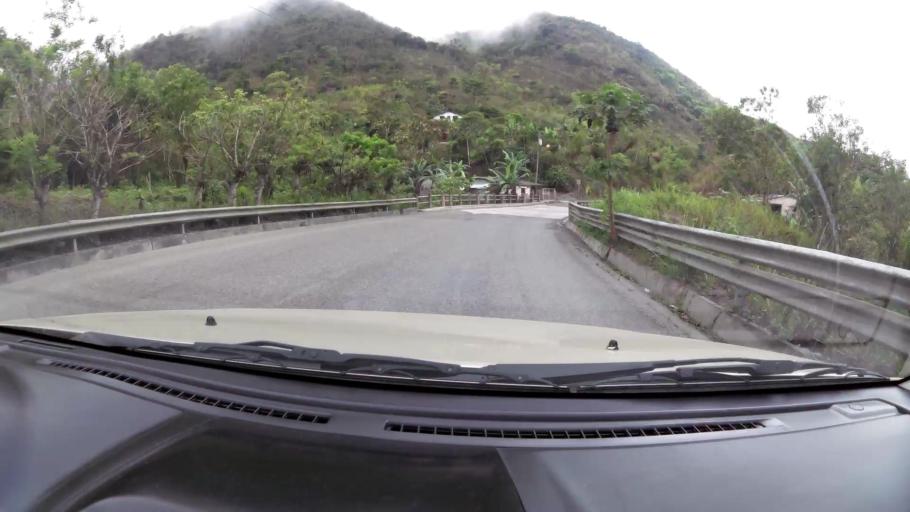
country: EC
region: El Oro
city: Pasaje
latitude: -3.3041
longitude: -79.5300
